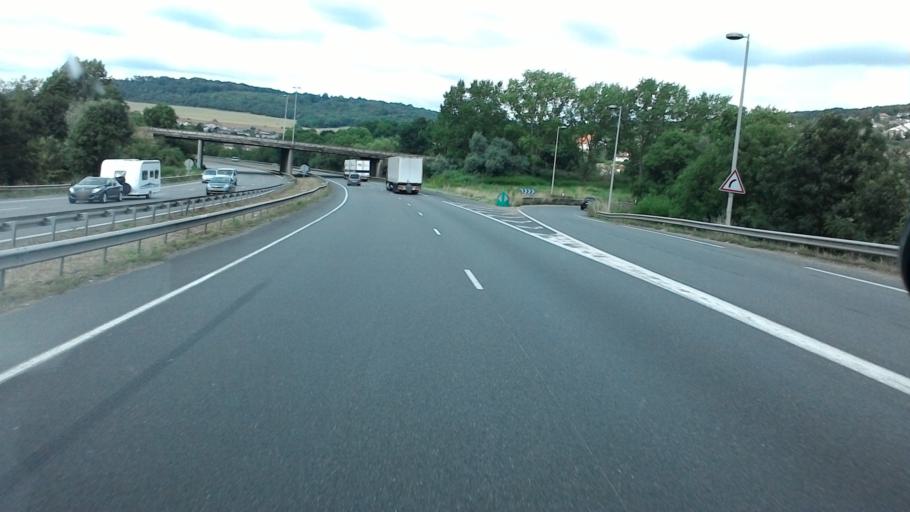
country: FR
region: Lorraine
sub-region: Departement de Meurthe-et-Moselle
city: Bouxieres-aux-Dames
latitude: 48.7496
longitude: 6.1568
